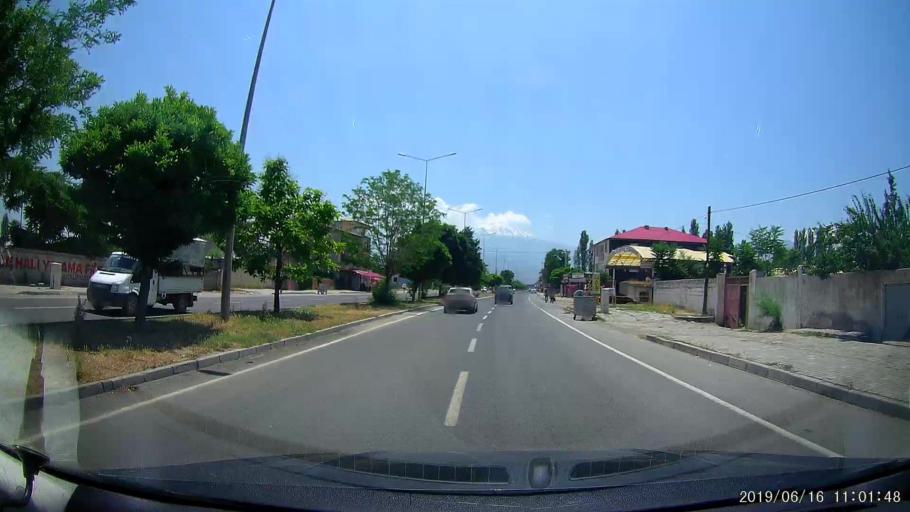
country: TR
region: Igdir
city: Igdir
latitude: 39.9125
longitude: 44.0536
